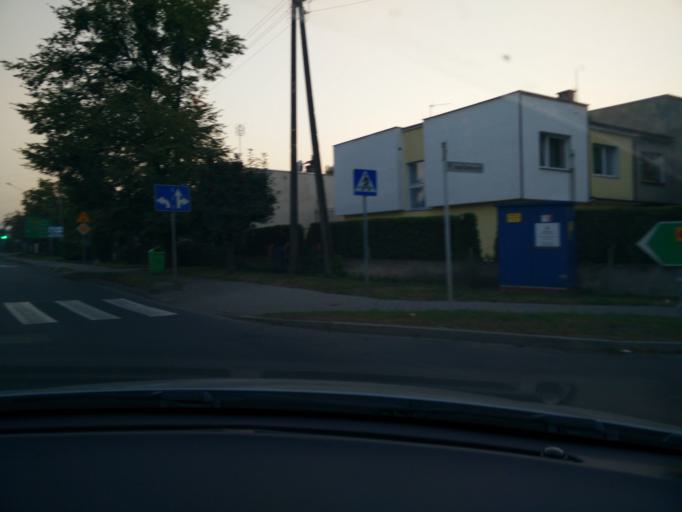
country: PL
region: Greater Poland Voivodeship
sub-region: Powiat sredzki
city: Sroda Wielkopolska
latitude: 52.2246
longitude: 17.2862
